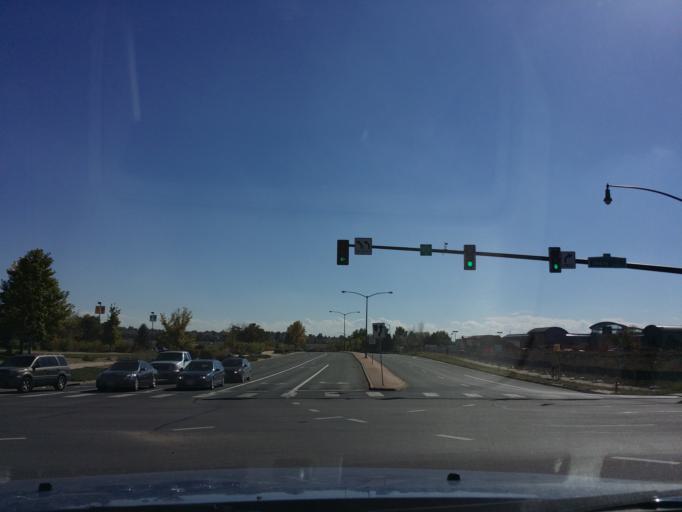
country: US
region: Colorado
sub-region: Broomfield County
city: Broomfield
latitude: 39.8882
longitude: -105.0673
